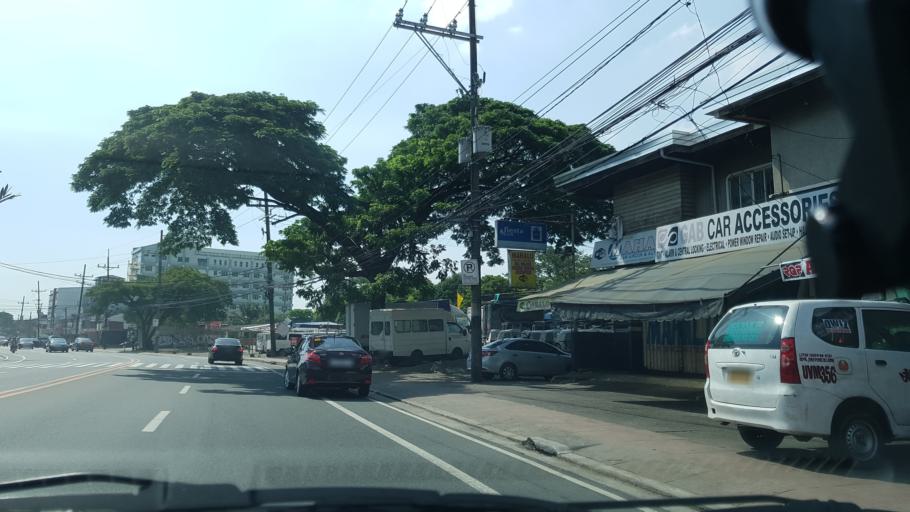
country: PH
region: Calabarzon
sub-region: Province of Rizal
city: Antipolo
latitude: 14.6511
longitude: 121.1096
